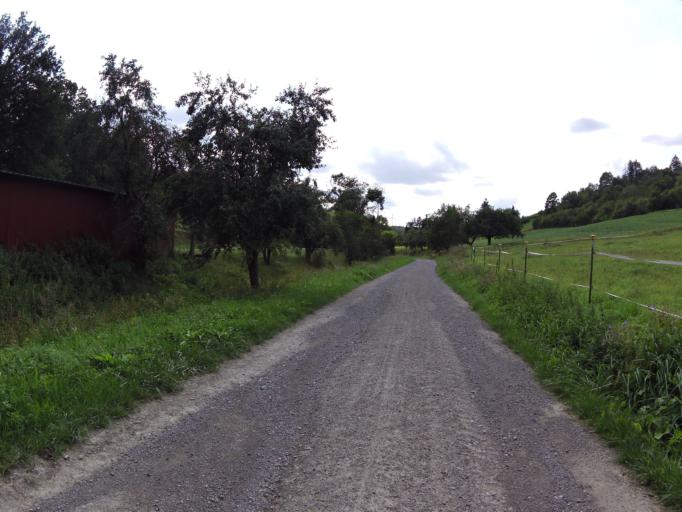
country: DE
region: Bavaria
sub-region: Regierungsbezirk Unterfranken
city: Erlabrunn
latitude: 49.8476
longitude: 9.8493
